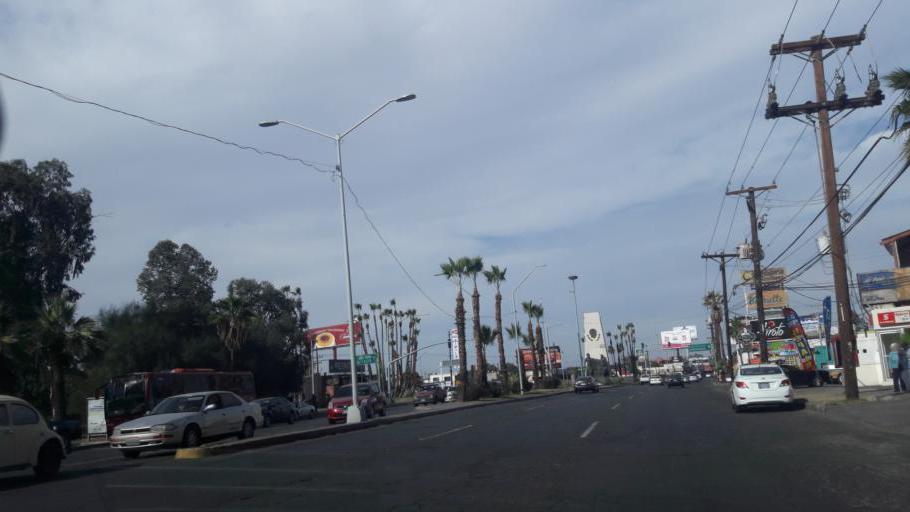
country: MX
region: Baja California
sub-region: Mexicali
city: Mexicali
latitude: 32.6462
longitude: -115.4516
